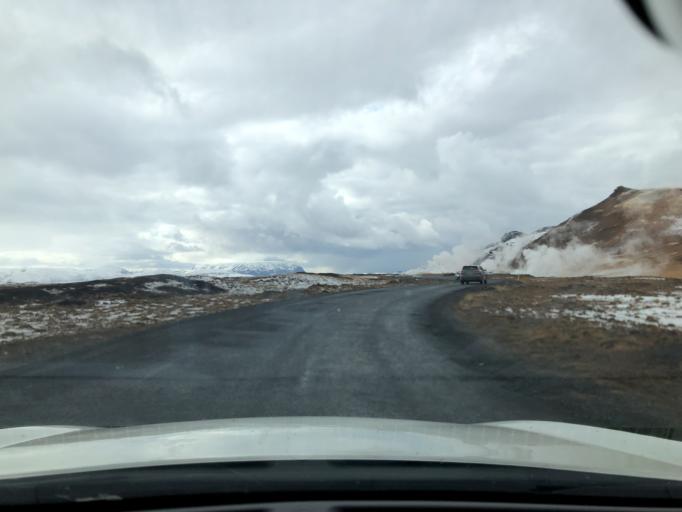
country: IS
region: Northeast
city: Laugar
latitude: 65.6442
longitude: -16.8042
